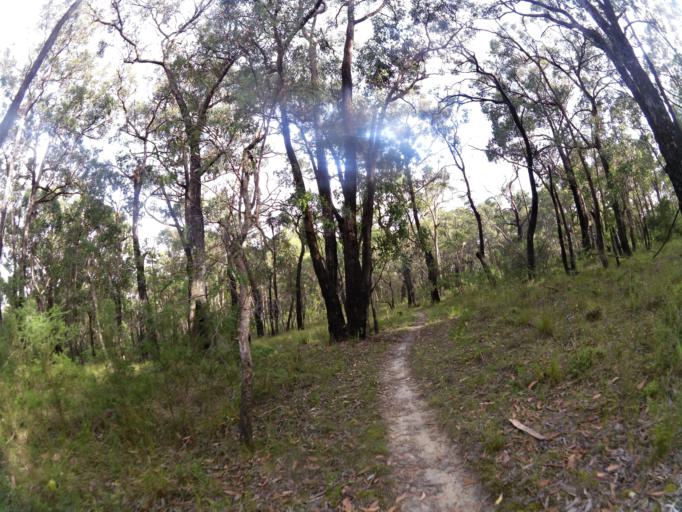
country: AU
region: Victoria
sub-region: Colac-Otway
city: Colac
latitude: -38.4891
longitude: 143.7160
